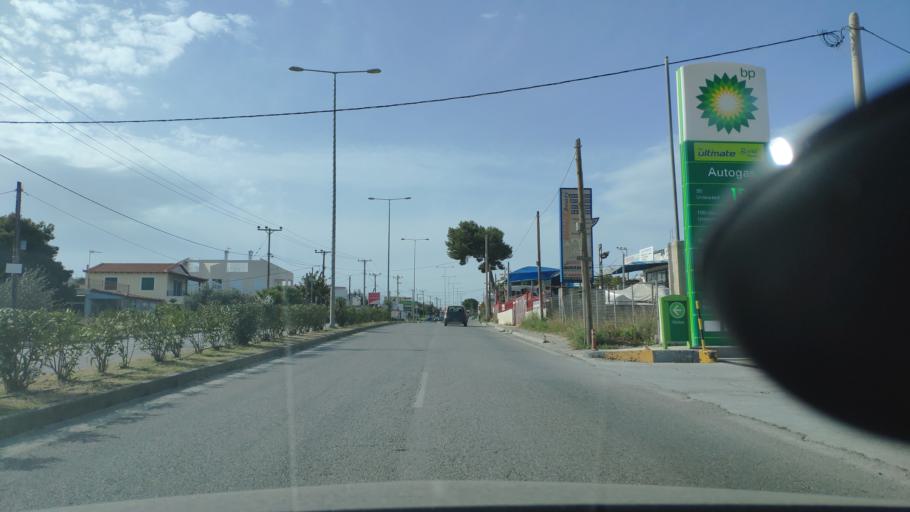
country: GR
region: Attica
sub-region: Nomarchia Anatolikis Attikis
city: Limin Mesoyaias
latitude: 37.8915
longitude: 23.9947
